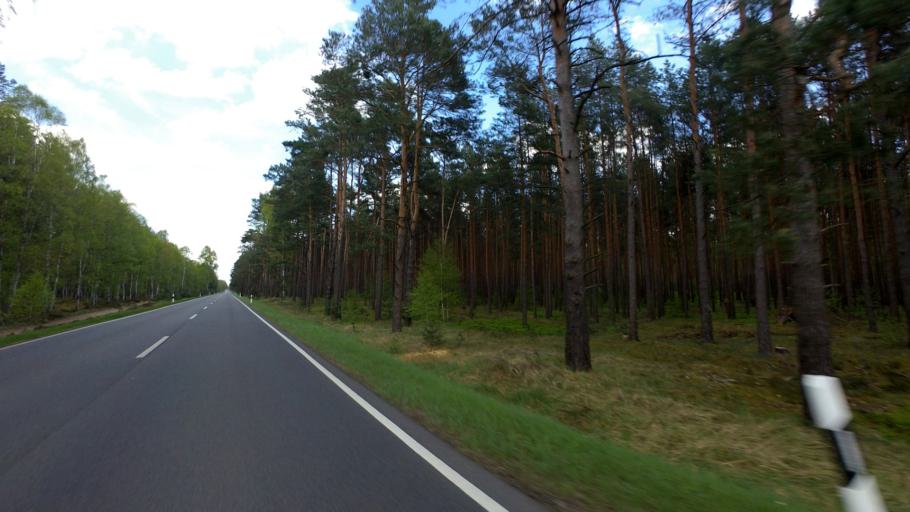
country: DE
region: Brandenburg
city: Marienwerder
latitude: 52.9562
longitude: 13.5665
